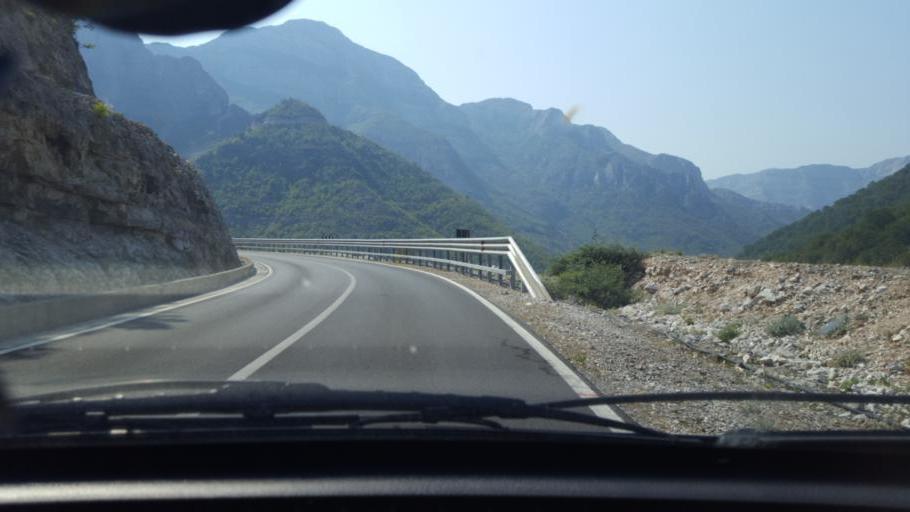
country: AL
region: Shkoder
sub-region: Rrethi i Malesia e Madhe
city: Kastrat
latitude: 42.4265
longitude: 19.5141
